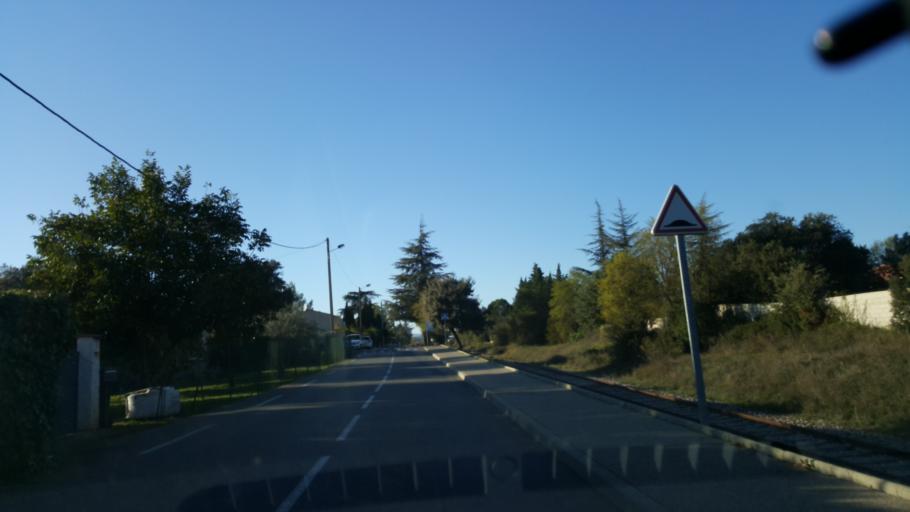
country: FR
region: Provence-Alpes-Cote d'Azur
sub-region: Departement du Var
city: Saint-Maximin-la-Sainte-Baume
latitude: 43.4483
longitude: 5.8564
